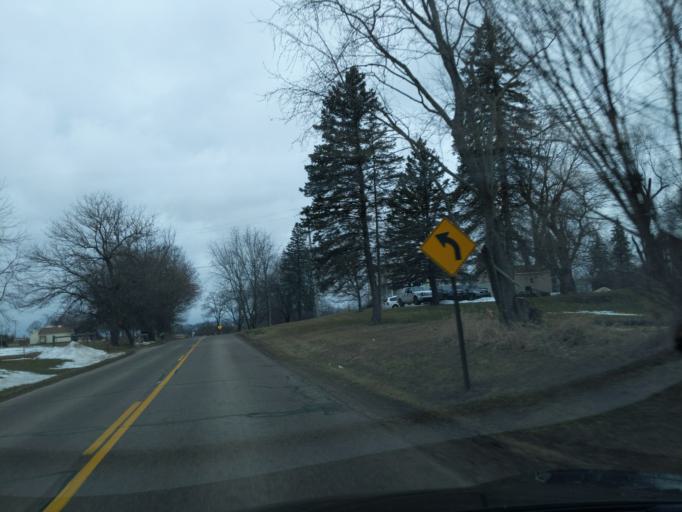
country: US
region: Michigan
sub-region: Eaton County
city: Eaton Rapids
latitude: 42.5374
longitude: -84.6295
